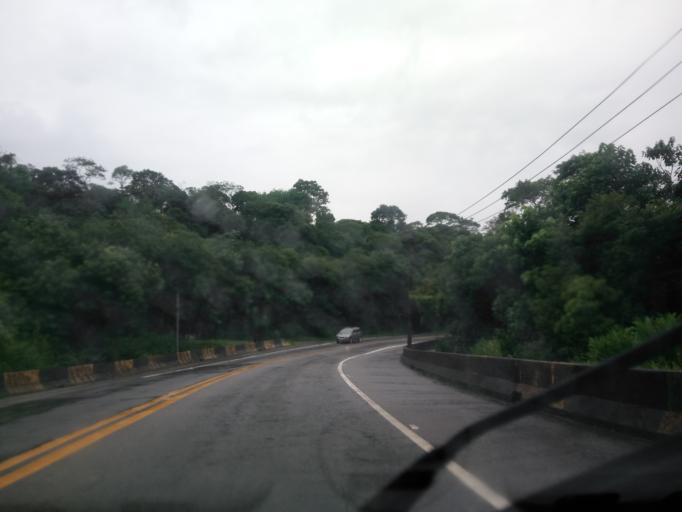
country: BR
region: Sao Paulo
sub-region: Sao Bernardo Do Campo
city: Sao Bernardo do Campo
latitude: -23.7861
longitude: -46.5077
